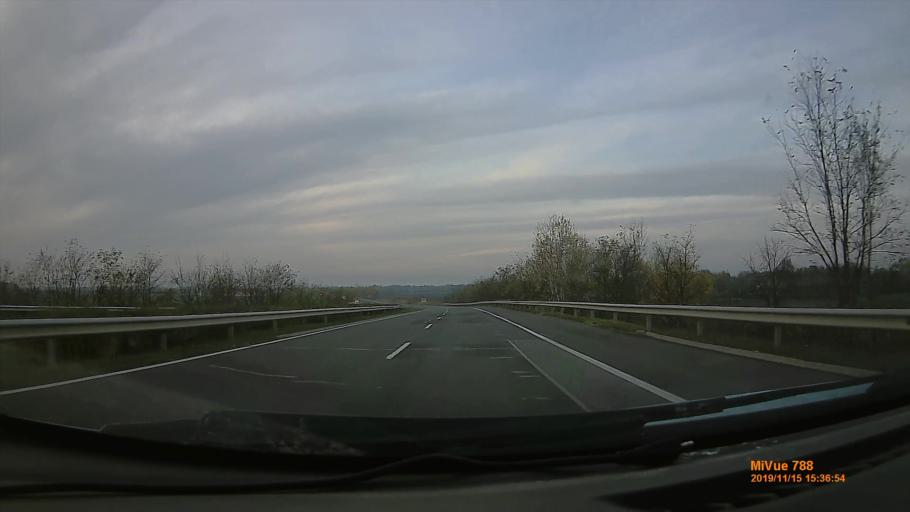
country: HU
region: Bekes
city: Gyula
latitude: 46.6602
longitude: 21.2055
